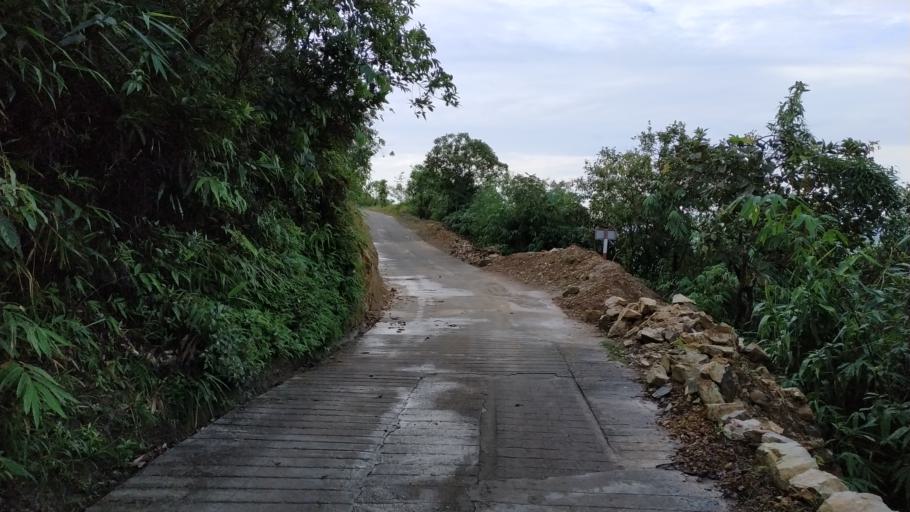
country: MM
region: Mon
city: Thaton
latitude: 16.9317
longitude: 97.3816
